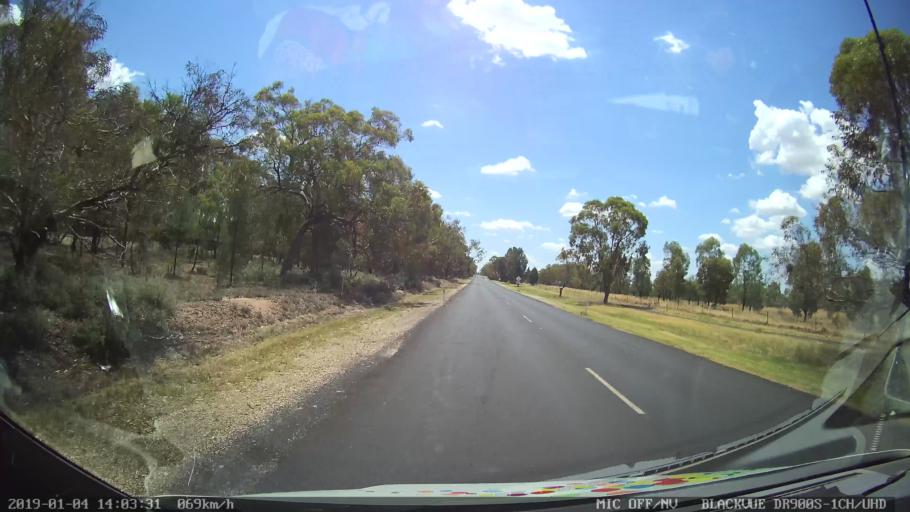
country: AU
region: New South Wales
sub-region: Dubbo Municipality
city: Dubbo
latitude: -32.2767
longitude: 148.5909
